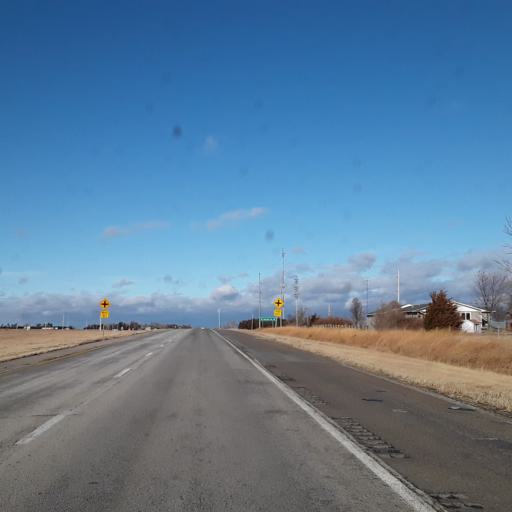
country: US
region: Kansas
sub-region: Republic County
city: Belleville
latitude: 39.8370
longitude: -97.6349
